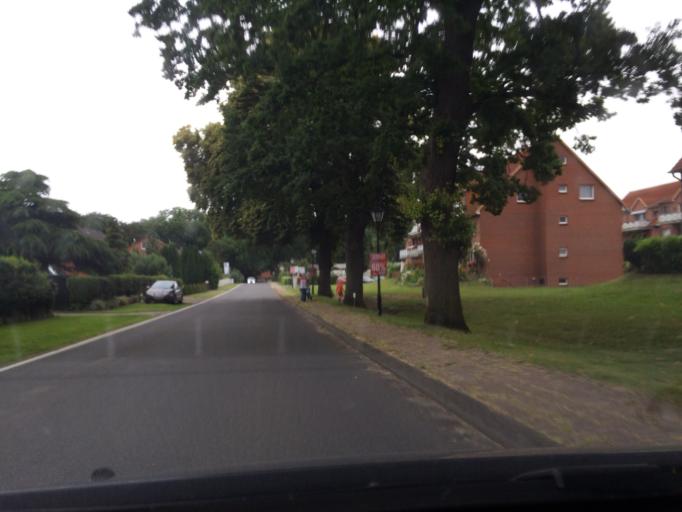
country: DE
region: Mecklenburg-Vorpommern
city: Prohn
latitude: 54.4018
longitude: 13.0118
